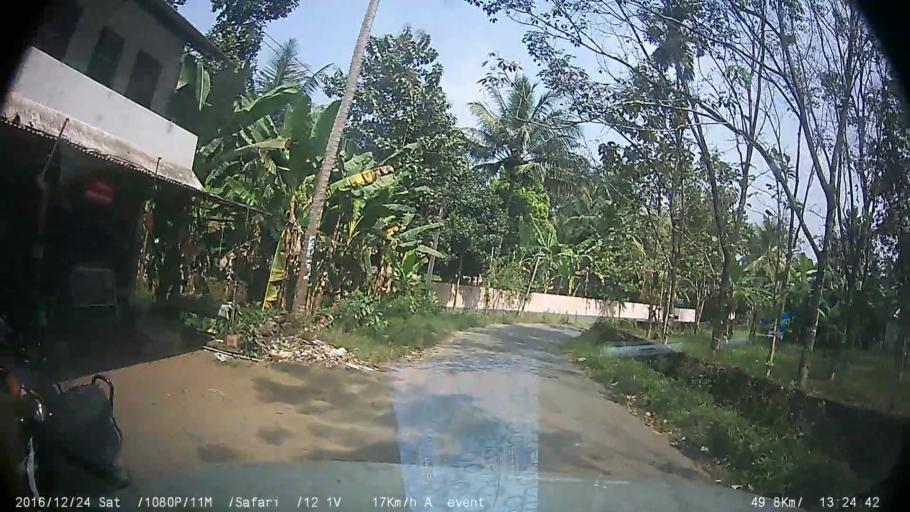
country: IN
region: Kerala
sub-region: Kottayam
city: Palackattumala
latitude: 9.8688
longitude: 76.6782
